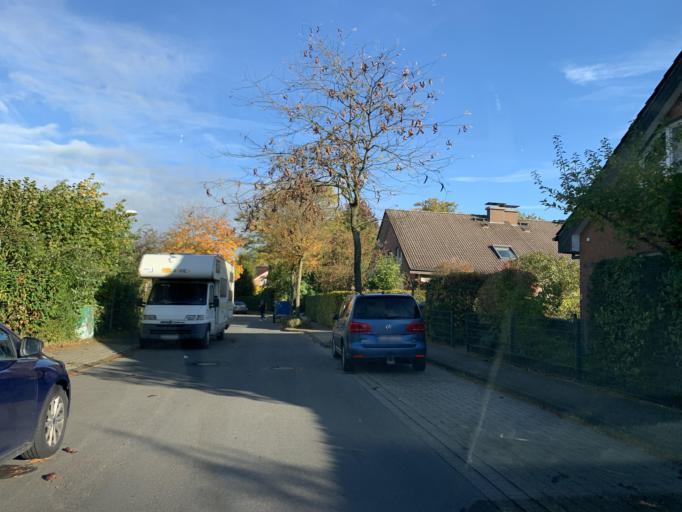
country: DE
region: North Rhine-Westphalia
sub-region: Regierungsbezirk Munster
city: Muenster
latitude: 51.9733
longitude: 7.5786
